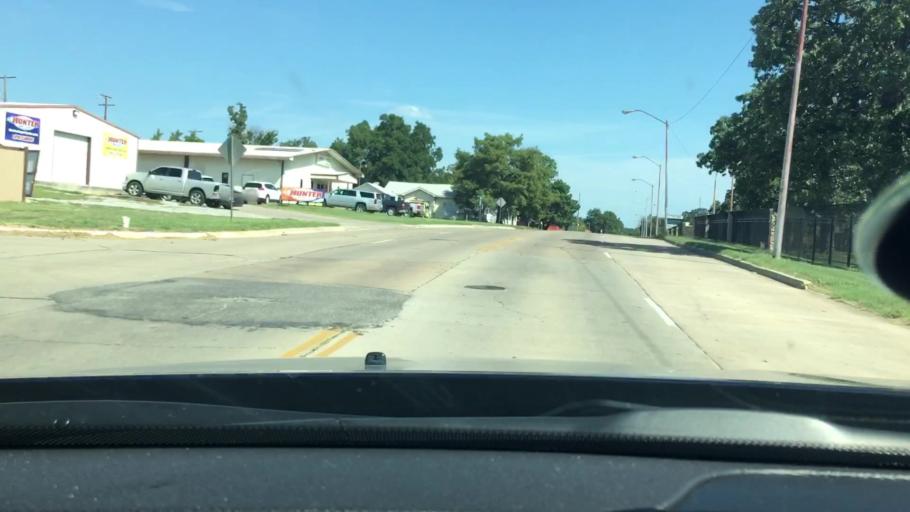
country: US
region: Oklahoma
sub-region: Carter County
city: Ardmore
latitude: 34.1596
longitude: -97.1215
